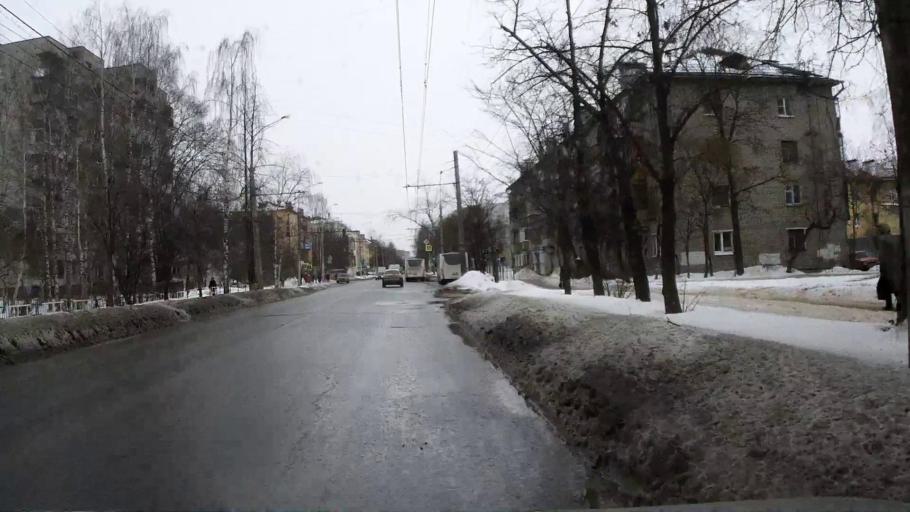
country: RU
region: Vologda
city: Vologda
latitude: 59.2271
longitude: 39.9014
